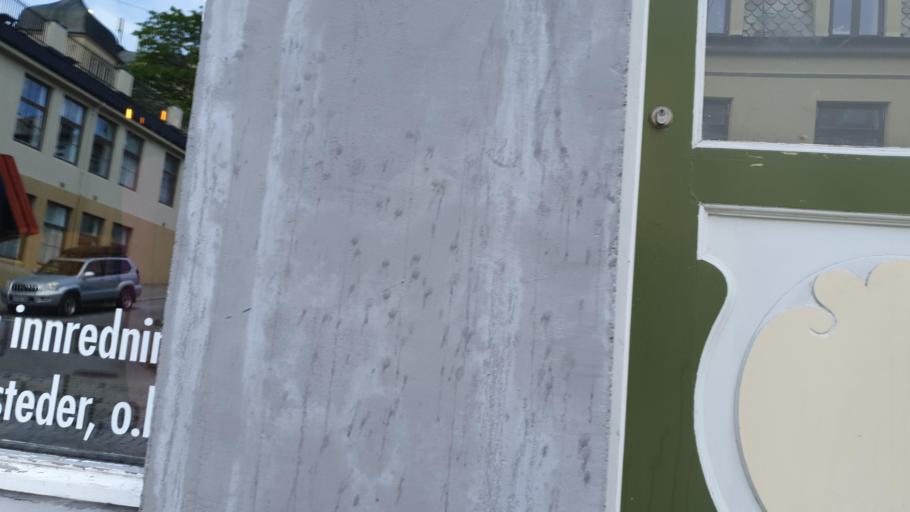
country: NO
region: More og Romsdal
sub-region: Alesund
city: Alesund
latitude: 62.4709
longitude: 6.1489
